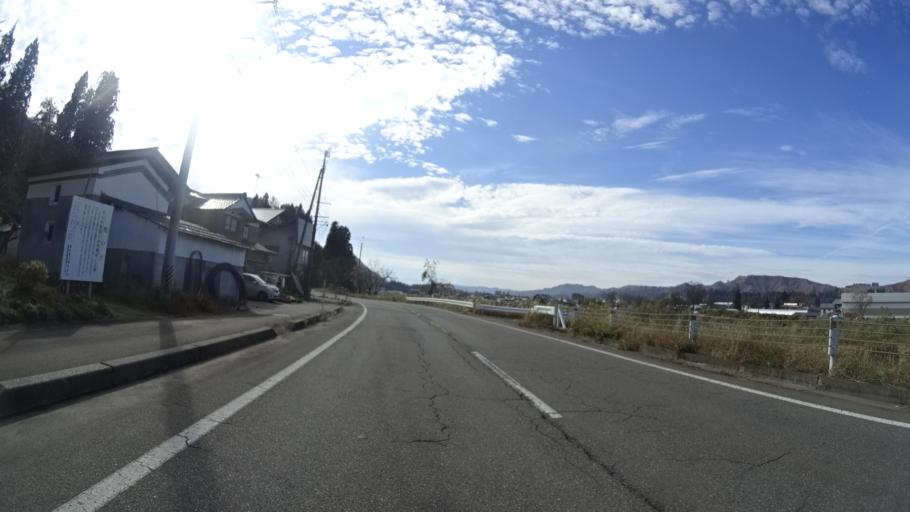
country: JP
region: Niigata
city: Ojiya
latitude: 37.2805
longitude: 138.9925
